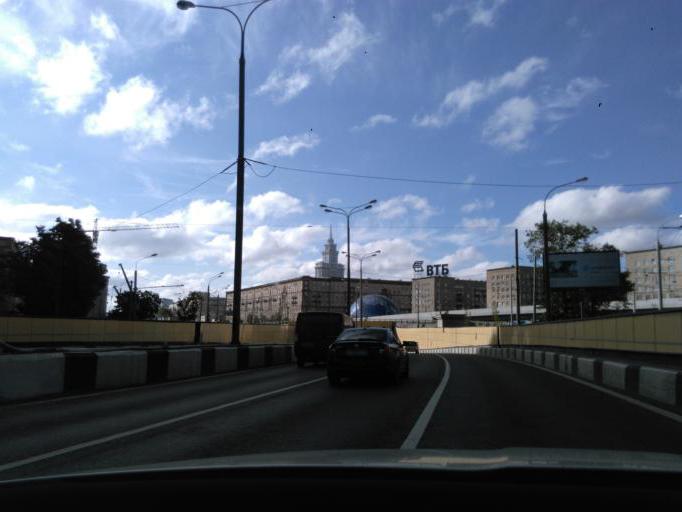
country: RU
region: Moscow
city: Sokol
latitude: 55.8080
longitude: 37.5067
